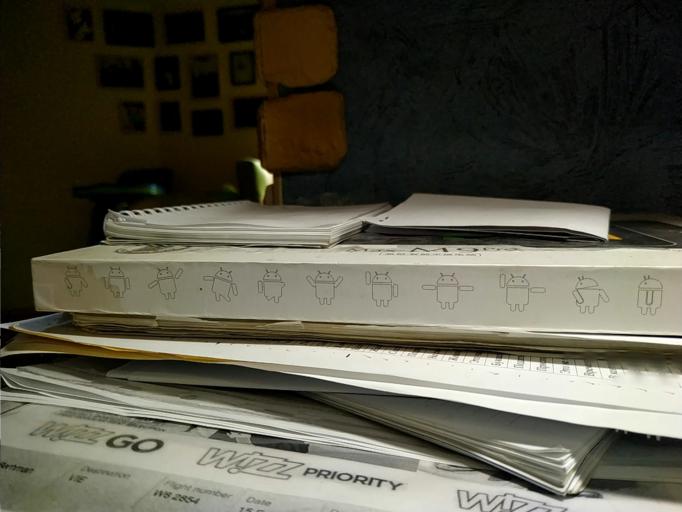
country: RU
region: Novgorod
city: Poddor'ye
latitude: 57.5237
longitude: 30.9130
